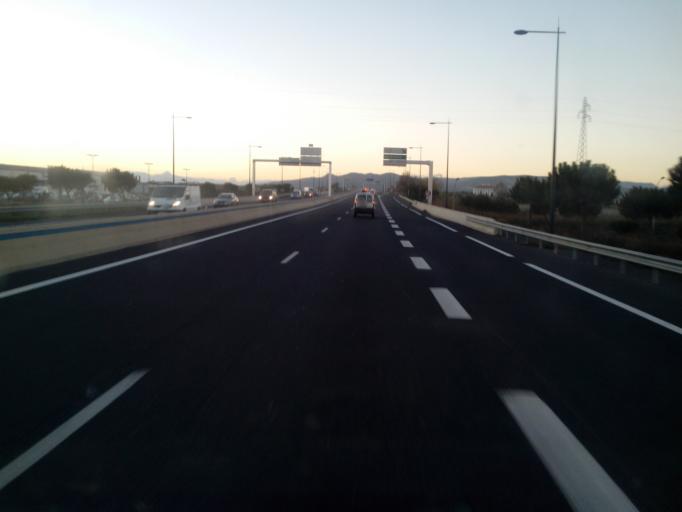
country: FR
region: Languedoc-Roussillon
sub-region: Departement des Pyrenees-Orientales
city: Pia
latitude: 42.7778
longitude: 2.9080
